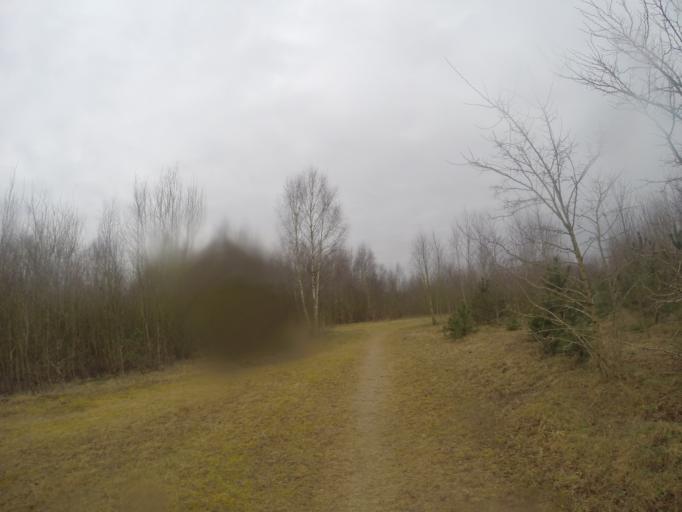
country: NL
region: Gelderland
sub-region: Gemeente Bronckhorst
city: Zelhem
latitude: 52.0182
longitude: 6.3297
